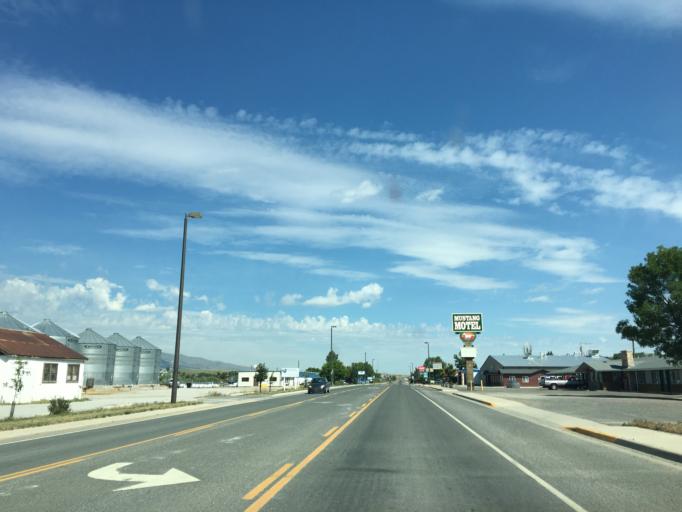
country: US
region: Montana
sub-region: Broadwater County
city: Townsend
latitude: 46.3229
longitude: -111.5239
